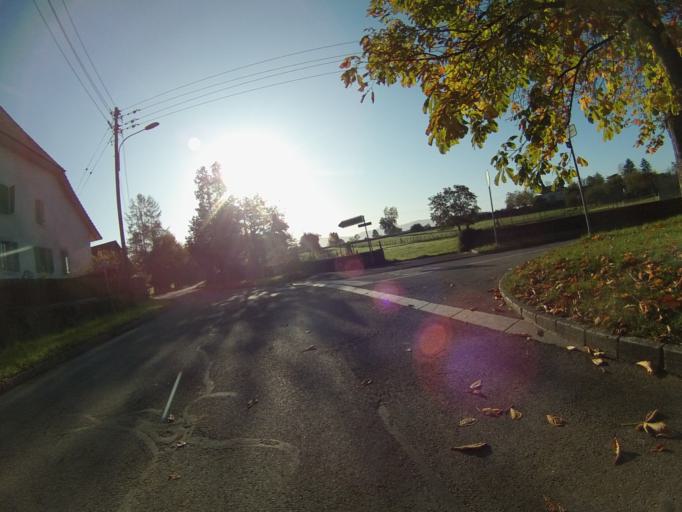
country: CH
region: Geneva
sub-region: Geneva
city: Meyrin
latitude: 46.2421
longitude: 6.0870
